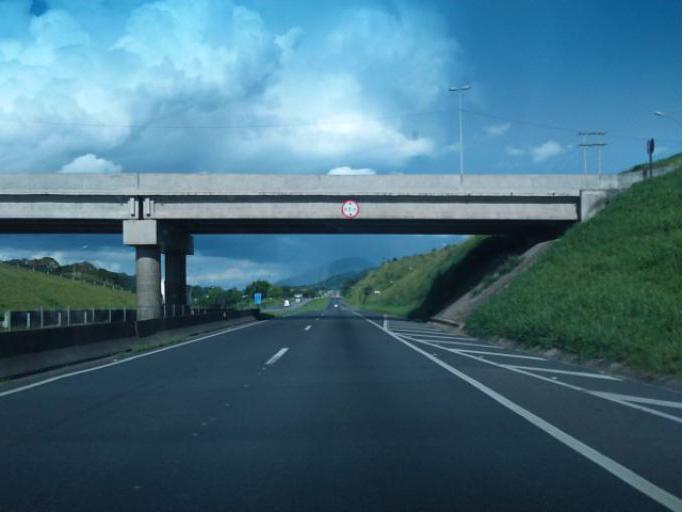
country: BR
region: Sao Paulo
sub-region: Juquia
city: Juquia
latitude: -24.3285
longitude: -47.5743
